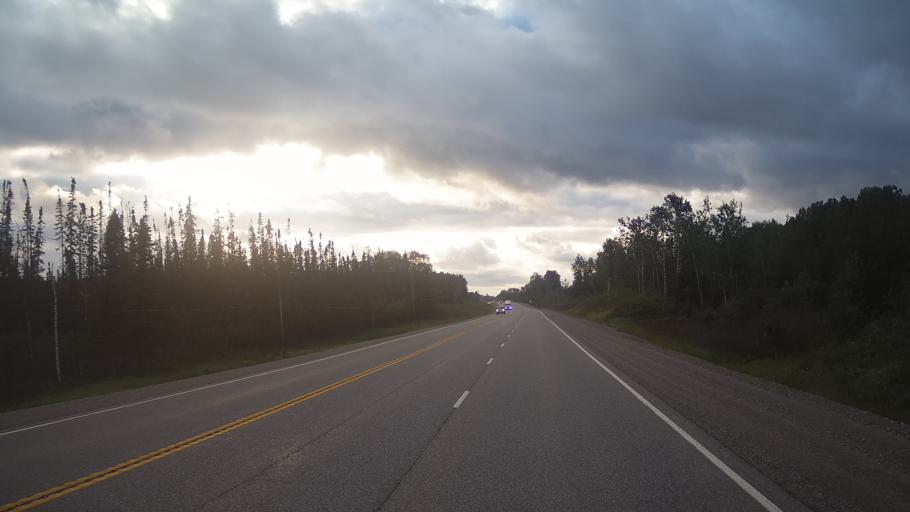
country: CA
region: Ontario
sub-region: Rainy River District
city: Atikokan
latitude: 49.0042
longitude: -90.4098
